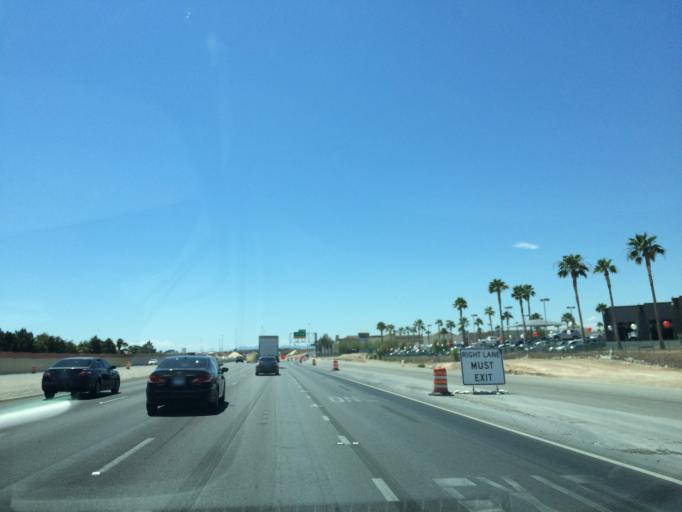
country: US
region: Nevada
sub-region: Clark County
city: Las Vegas
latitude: 36.2694
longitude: -115.2597
